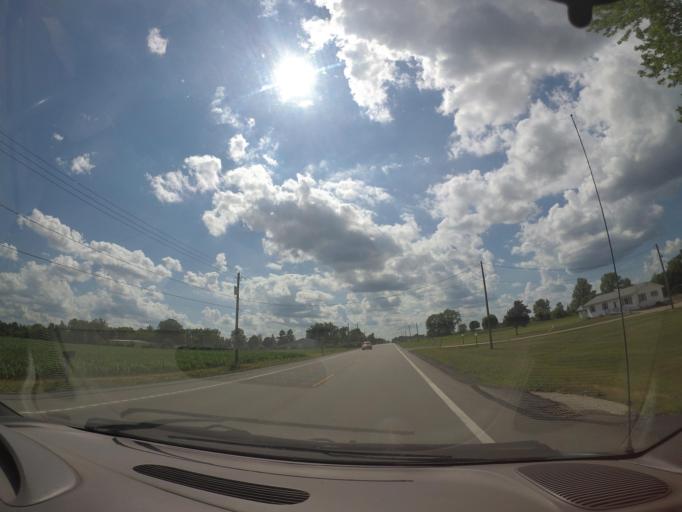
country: US
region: Ohio
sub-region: Huron County
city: Norwalk
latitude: 41.2493
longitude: -82.5463
